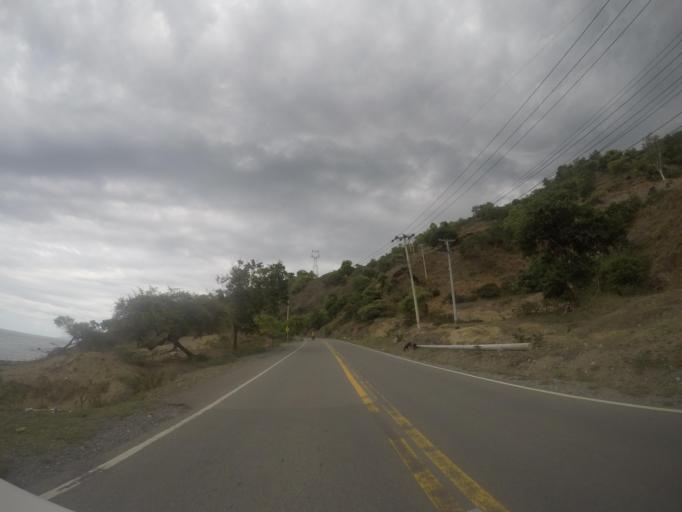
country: TL
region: Liquica
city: Liquica
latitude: -8.5768
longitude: 125.3700
